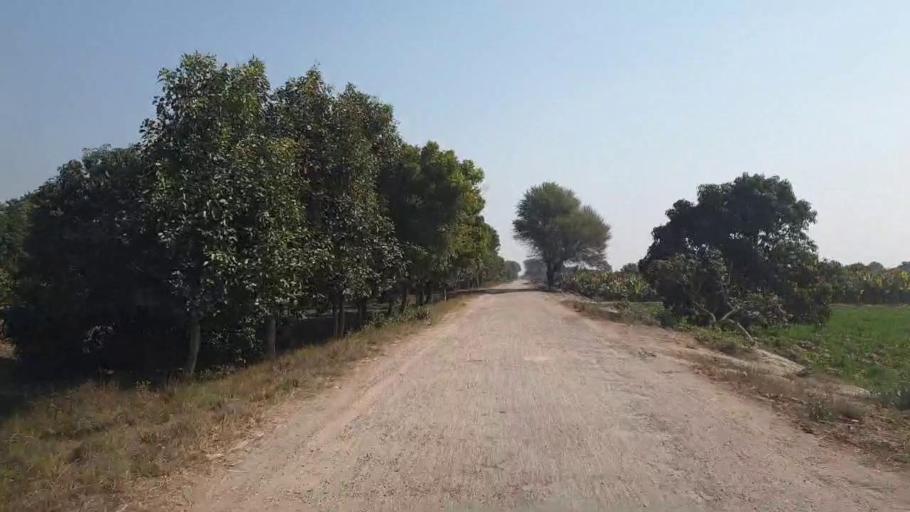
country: PK
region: Sindh
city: Tando Jam
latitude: 25.3424
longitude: 68.5952
